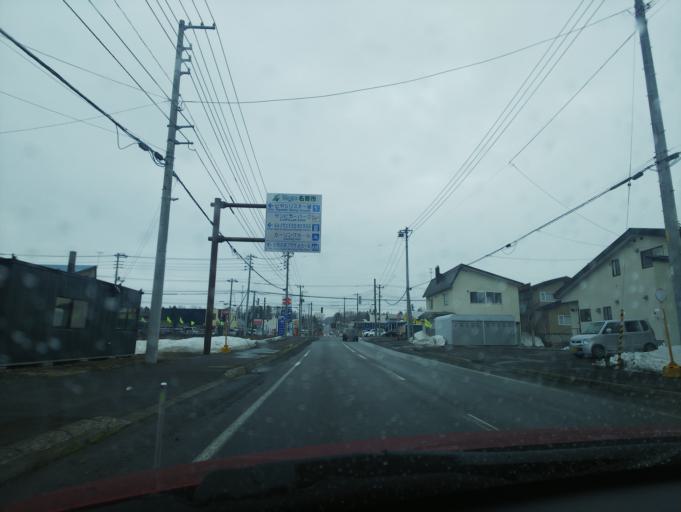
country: JP
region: Hokkaido
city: Nayoro
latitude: 44.3363
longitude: 142.4633
